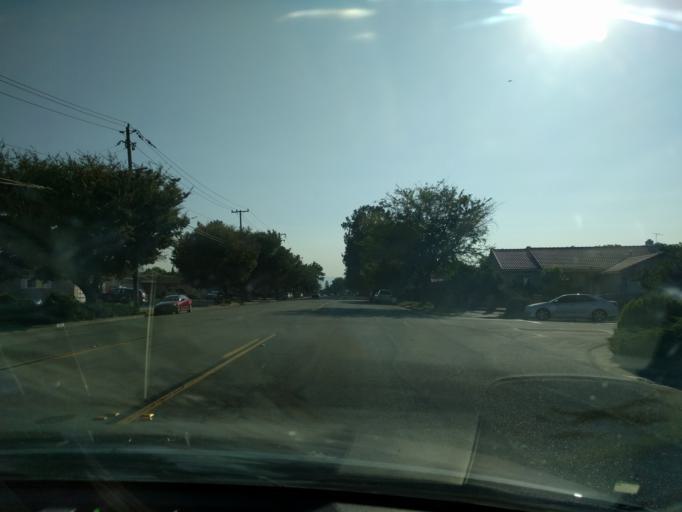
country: US
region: California
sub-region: Santa Clara County
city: East Foothills
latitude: 37.3957
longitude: -121.8560
